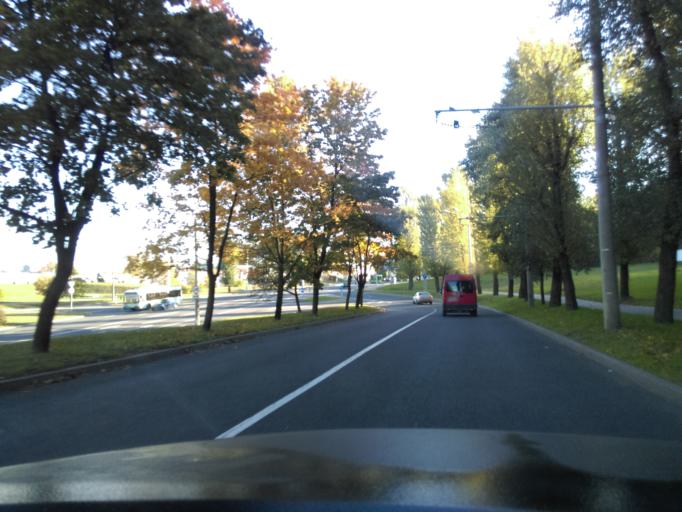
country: BY
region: Minsk
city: Minsk
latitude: 53.8850
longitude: 27.6216
